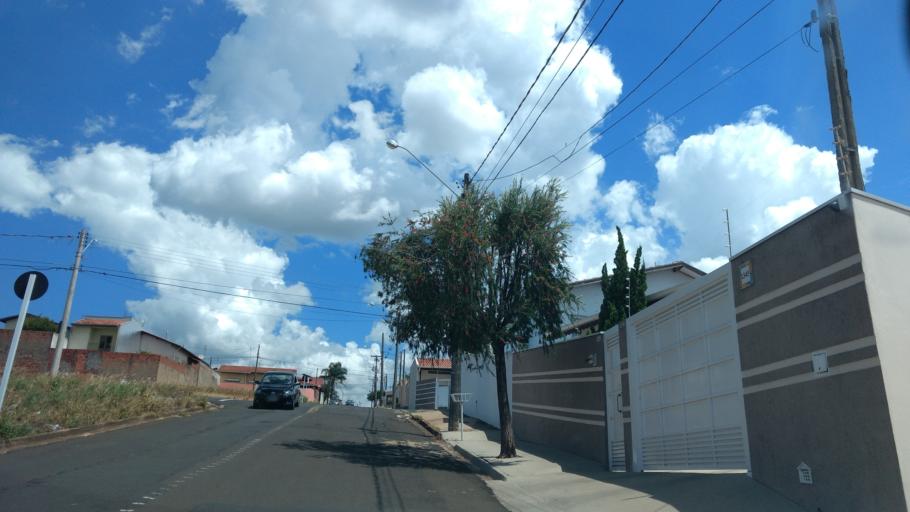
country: BR
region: Sao Paulo
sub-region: Botucatu
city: Botucatu
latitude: -22.8638
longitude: -48.4545
